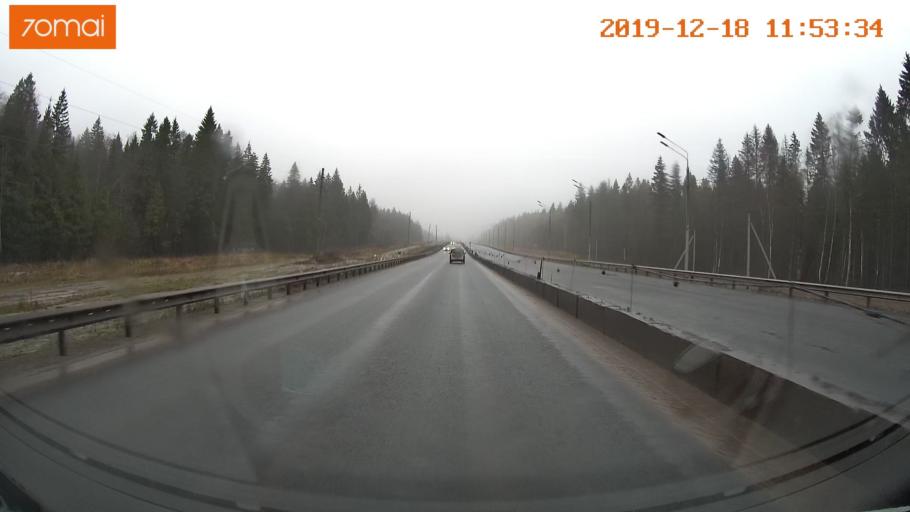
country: RU
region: Moskovskaya
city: Yershovo
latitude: 55.8058
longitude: 36.9197
